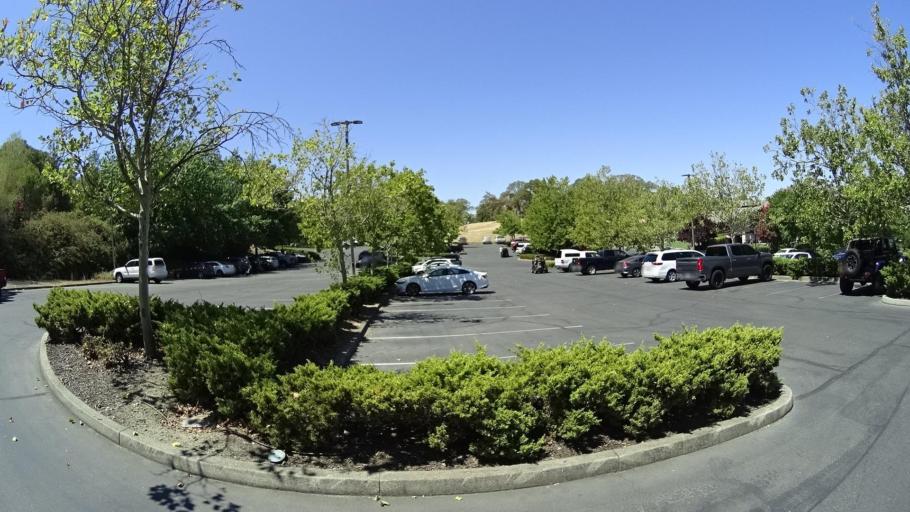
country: US
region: California
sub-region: Placer County
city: Rocklin
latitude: 38.8247
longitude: -121.2409
